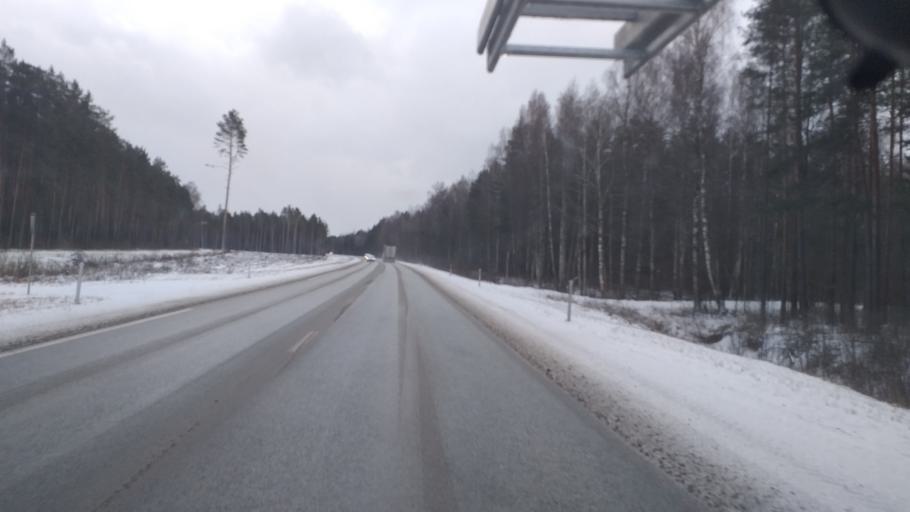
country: LV
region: Babite
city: Pinki
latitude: 56.9070
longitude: 23.9180
